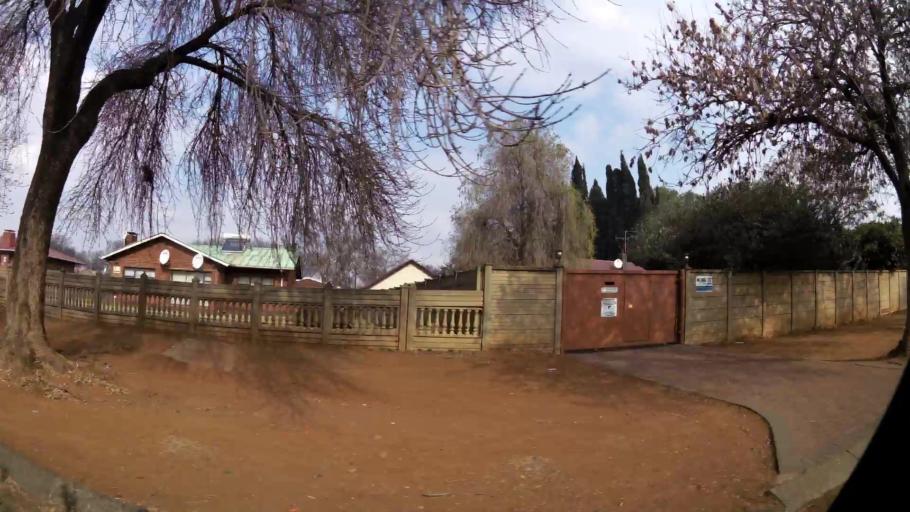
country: ZA
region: Gauteng
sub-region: Sedibeng District Municipality
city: Vanderbijlpark
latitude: -26.6885
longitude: 27.8450
